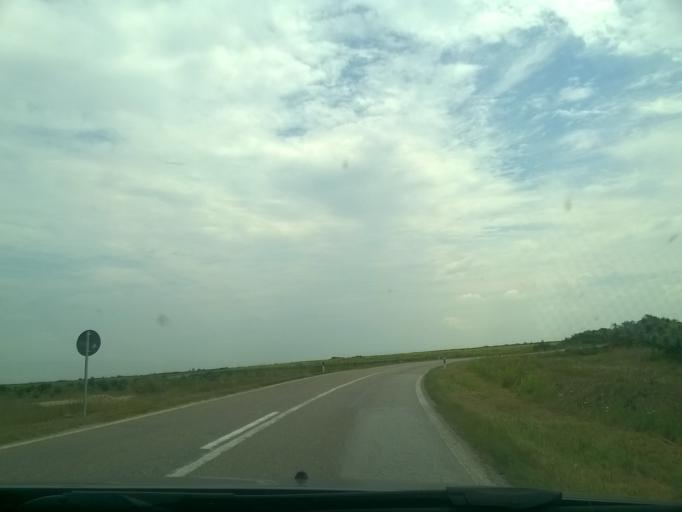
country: RS
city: Konak
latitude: 45.3048
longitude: 20.9195
